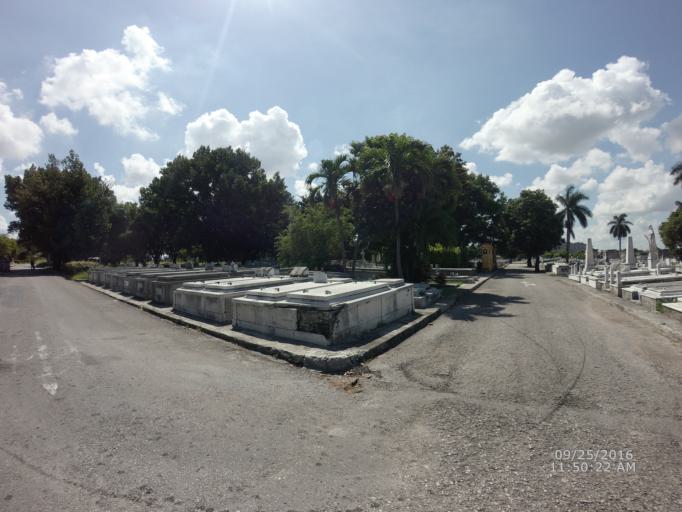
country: CU
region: La Habana
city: Havana
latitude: 23.1244
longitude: -82.3948
